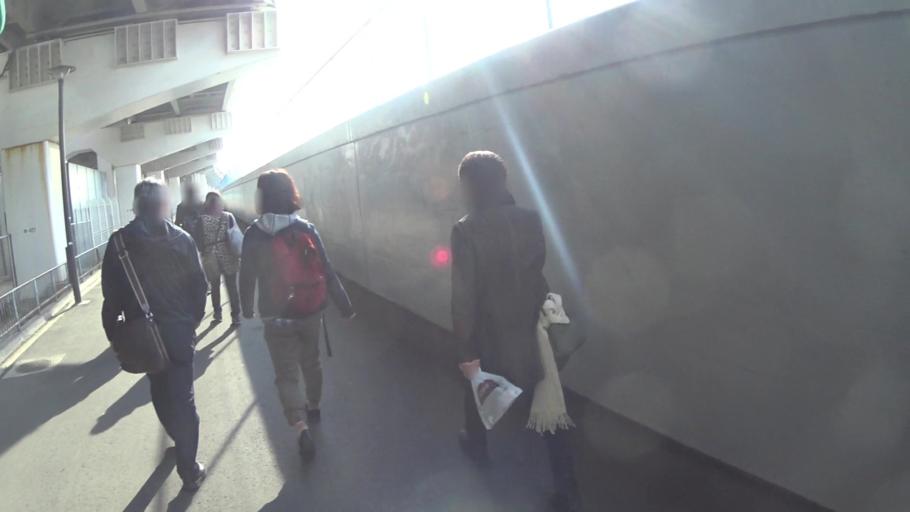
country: JP
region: Saitama
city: Soka
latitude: 35.7255
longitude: 139.8101
